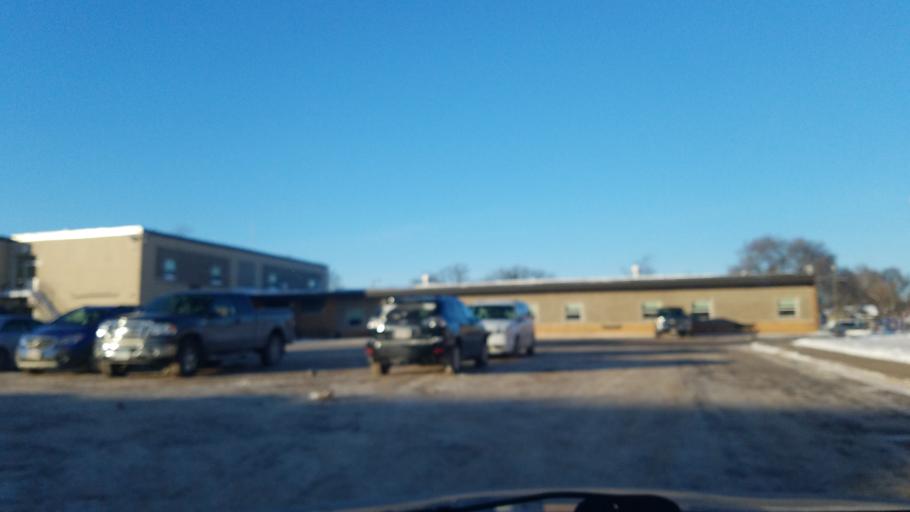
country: US
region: Wisconsin
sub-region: Barron County
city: Rice Lake
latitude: 45.5044
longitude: -91.7376
